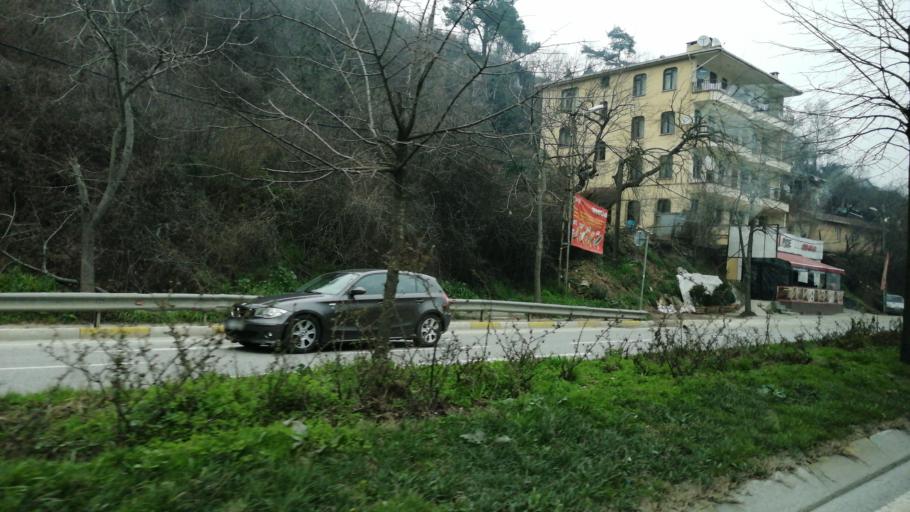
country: TR
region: Istanbul
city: Umraniye
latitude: 41.0824
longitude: 29.0825
